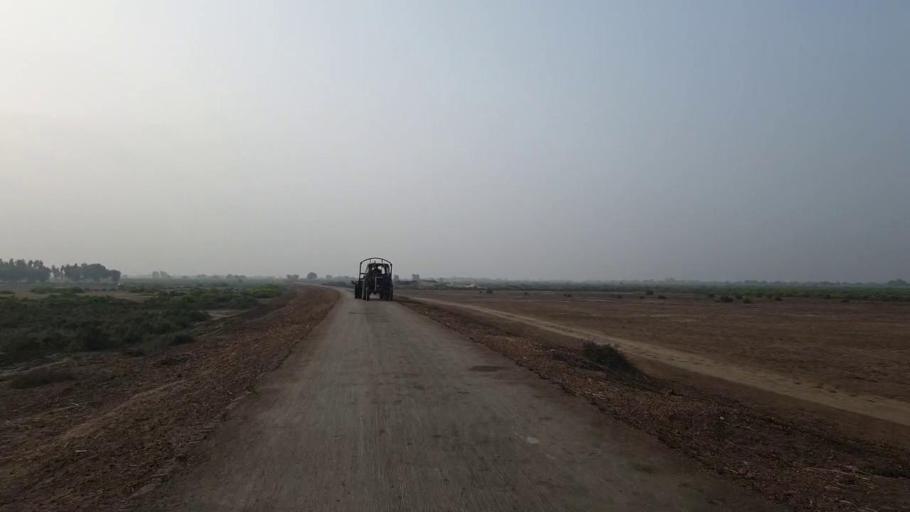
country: PK
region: Sindh
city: Tando Muhammad Khan
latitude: 25.1602
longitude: 68.6099
